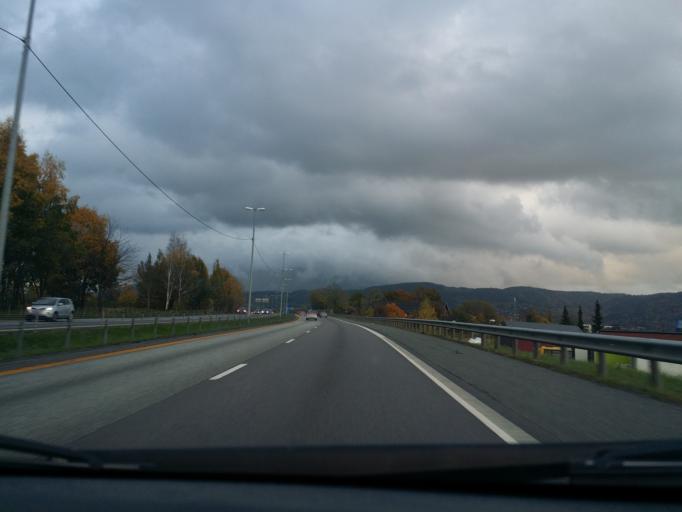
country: NO
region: Buskerud
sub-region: Lier
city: Lierbyen
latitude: 59.7516
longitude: 10.2453
